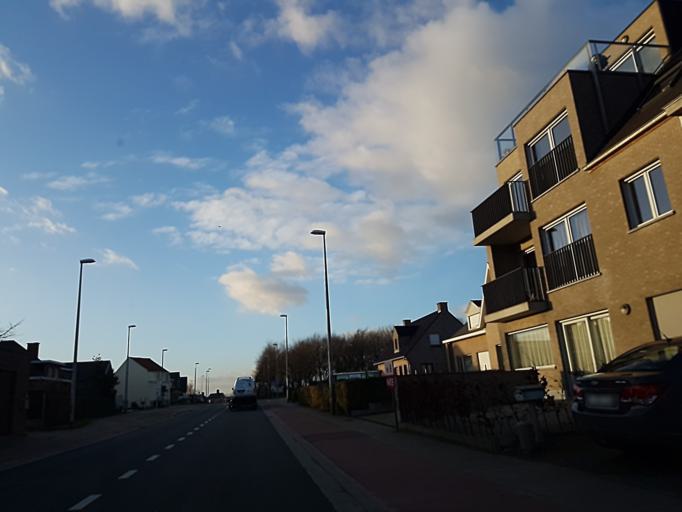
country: BE
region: Flanders
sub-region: Provincie Oost-Vlaanderen
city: Kruishoutem
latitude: 50.9069
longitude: 3.5189
